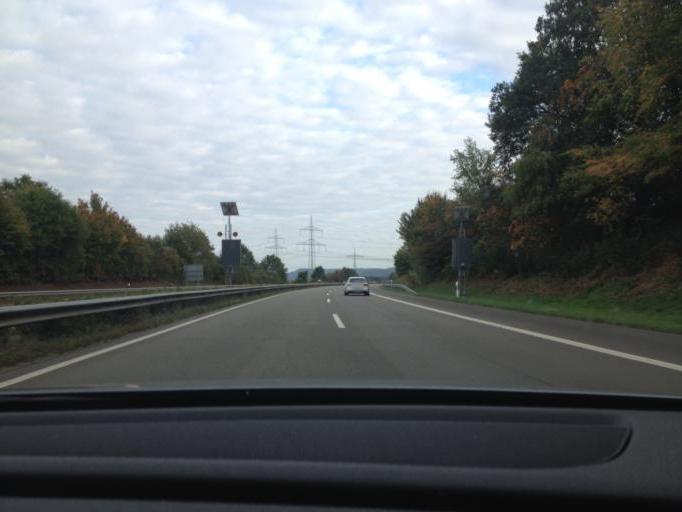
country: DE
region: Rheinland-Pfalz
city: Hutschenhausen
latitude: 49.4420
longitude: 7.5018
